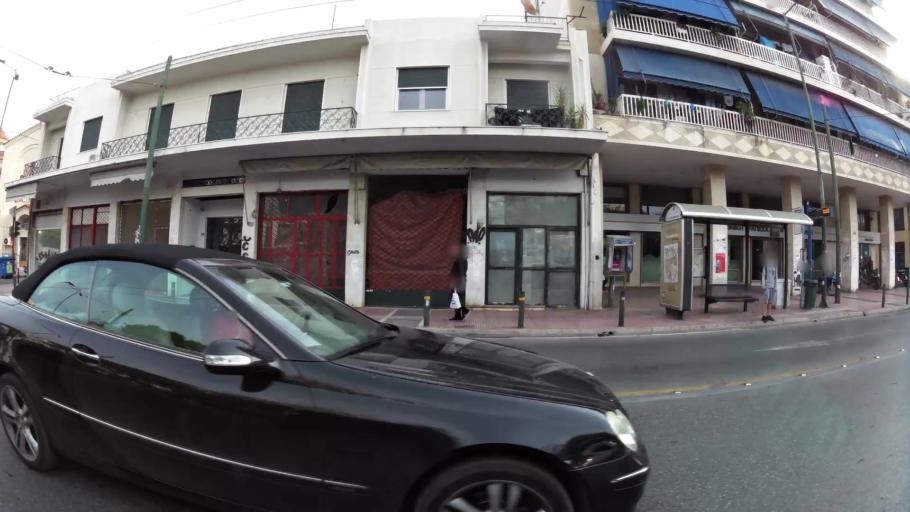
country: GR
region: Attica
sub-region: Nomarchia Athinas
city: Athens
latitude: 37.9924
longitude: 23.7140
